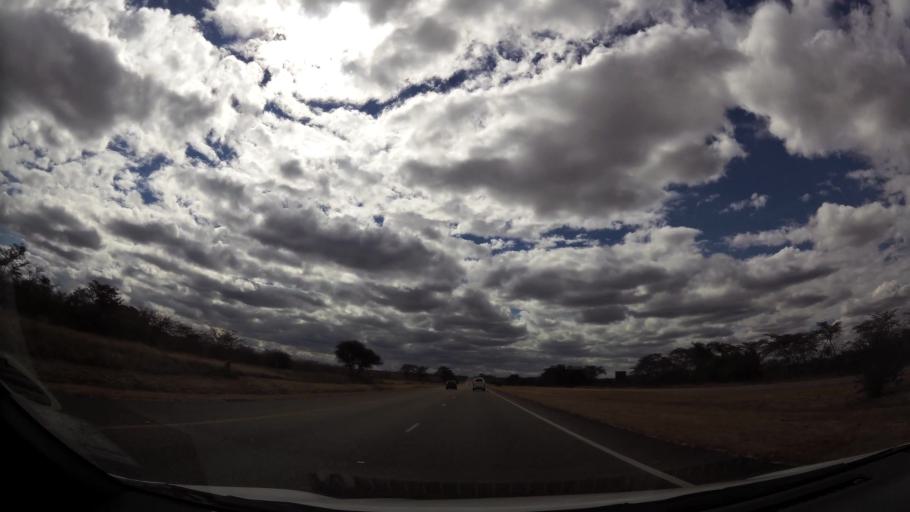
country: ZA
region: Limpopo
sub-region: Waterberg District Municipality
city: Bela-Bela
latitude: -24.8940
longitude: 28.3814
